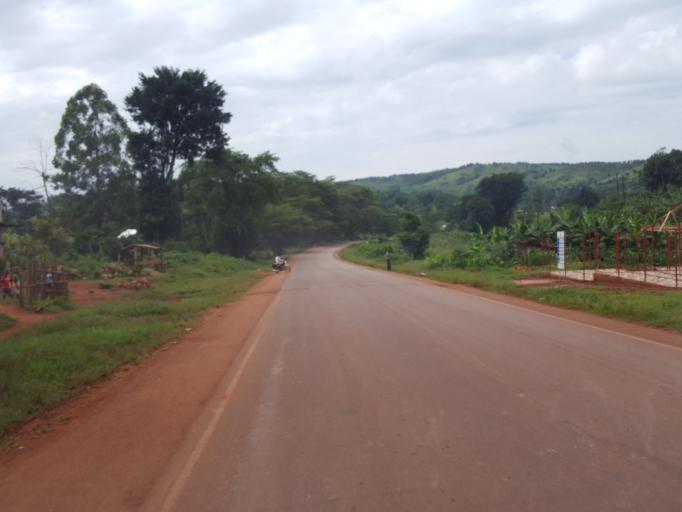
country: UG
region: Central Region
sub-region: Mityana District
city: Mityana
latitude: 0.6317
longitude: 32.1138
